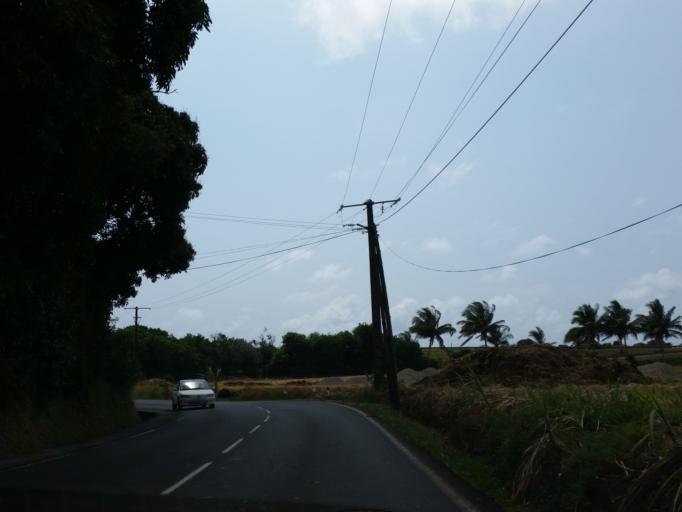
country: RE
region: Reunion
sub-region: Reunion
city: Sainte-Suzanne
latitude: -20.9177
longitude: 55.6189
